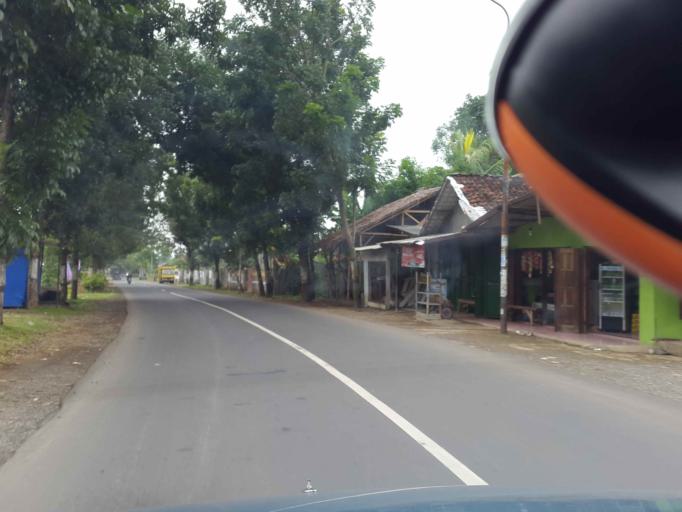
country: ID
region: Central Java
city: Wonopringgo
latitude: -7.0113
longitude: 109.6337
